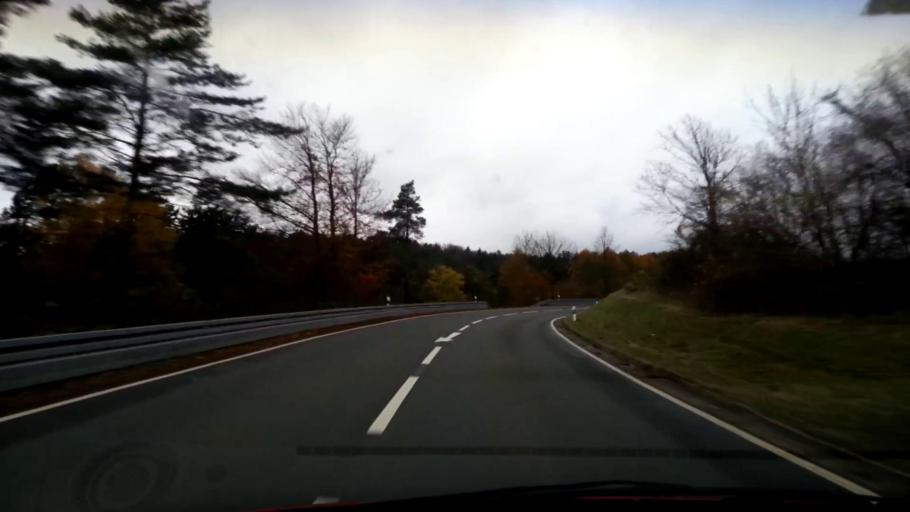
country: DE
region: Bavaria
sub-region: Upper Franconia
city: Poxdorf
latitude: 49.9222
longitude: 11.0810
